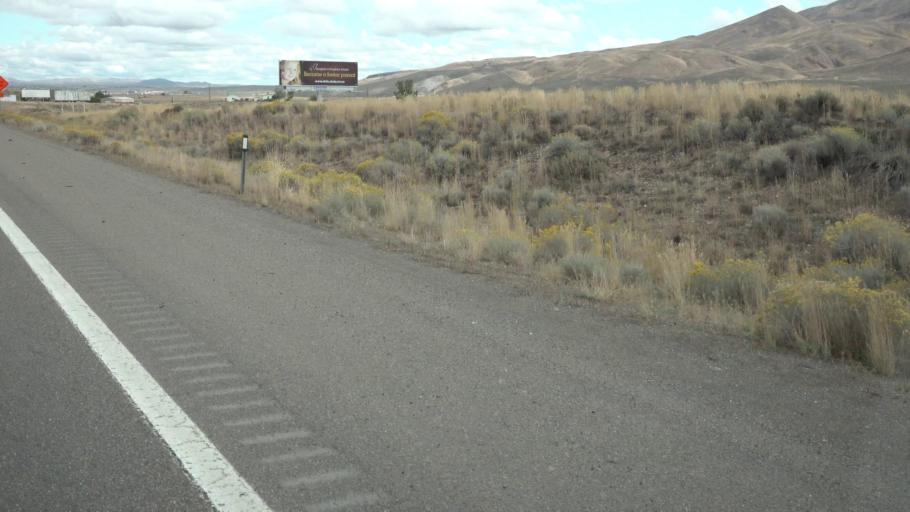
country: US
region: Nevada
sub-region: Elko County
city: Elko
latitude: 40.8979
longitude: -115.7072
